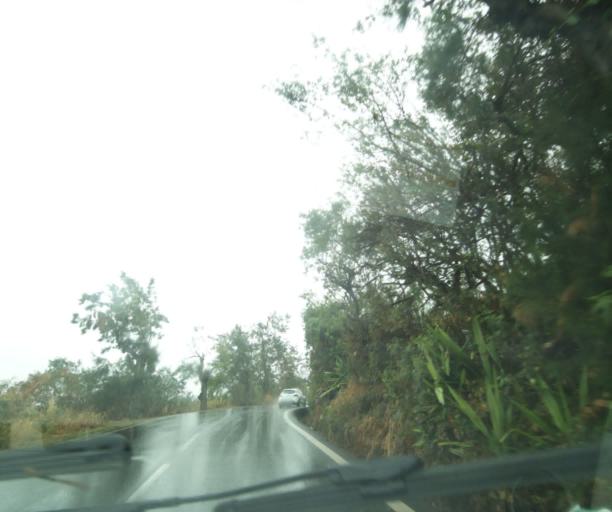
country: RE
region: Reunion
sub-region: Reunion
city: Saint-Paul
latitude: -21.0321
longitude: 55.2826
